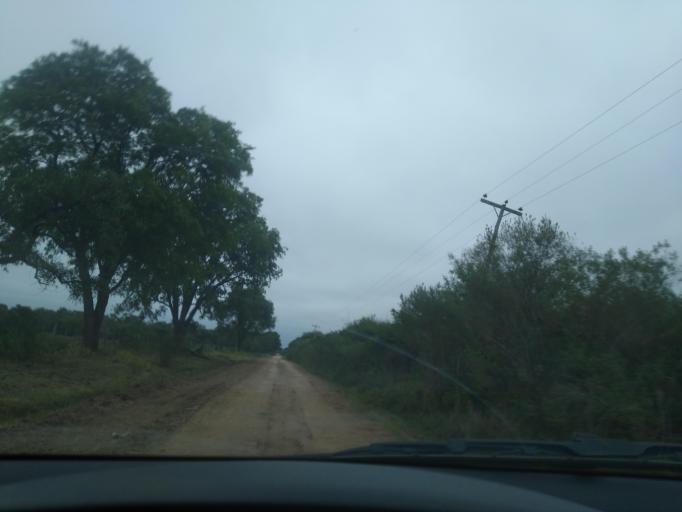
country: AR
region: Chaco
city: Colonia Benitez
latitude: -27.3569
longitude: -58.9631
